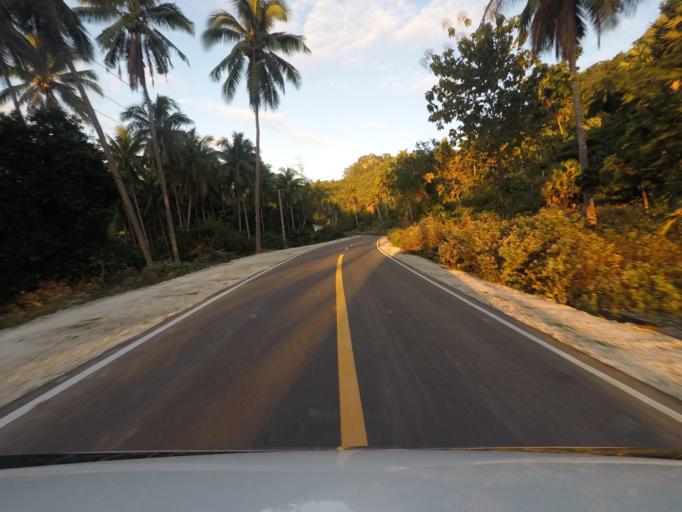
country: TL
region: Lautem
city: Lospalos
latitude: -8.3980
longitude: 127.2690
